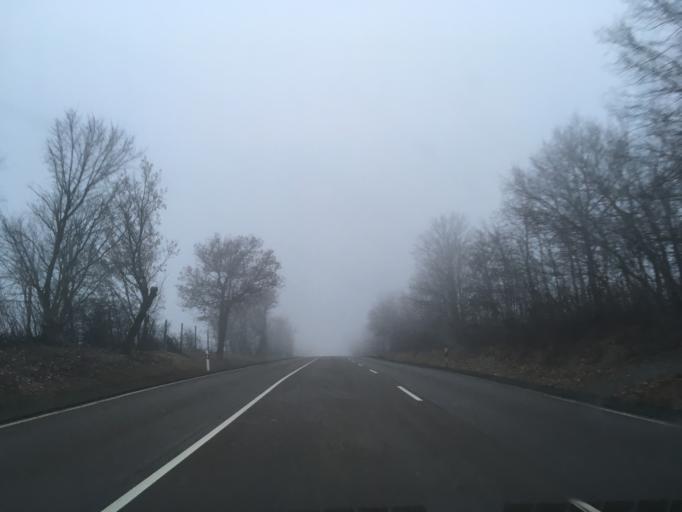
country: HU
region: Heves
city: Eger
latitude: 47.8659
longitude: 20.3793
